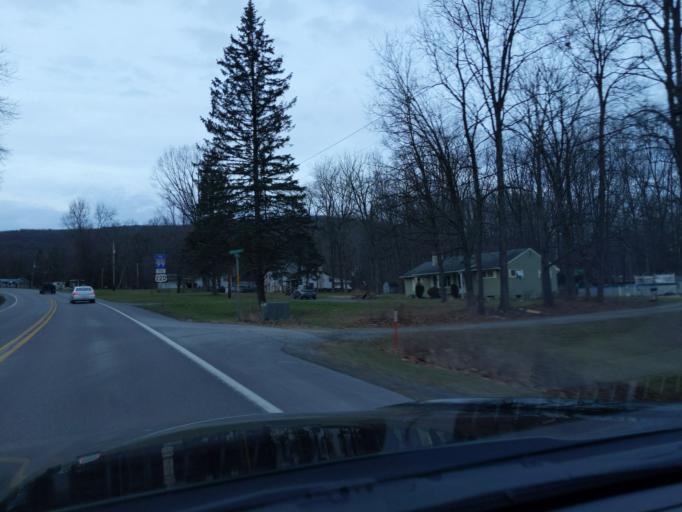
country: US
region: Pennsylvania
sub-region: Blair County
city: Lakemont
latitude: 40.4564
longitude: -78.3549
